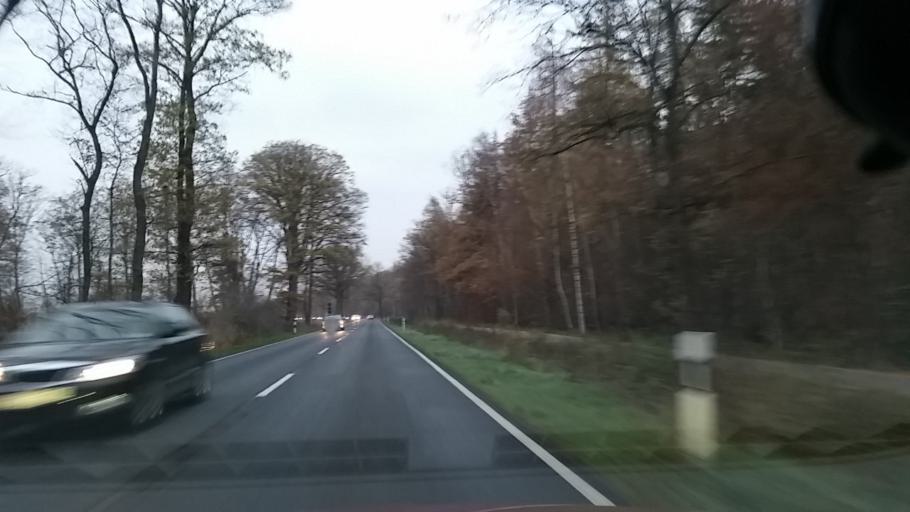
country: DE
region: Lower Saxony
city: Wolfsburg
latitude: 52.3782
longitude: 10.7426
